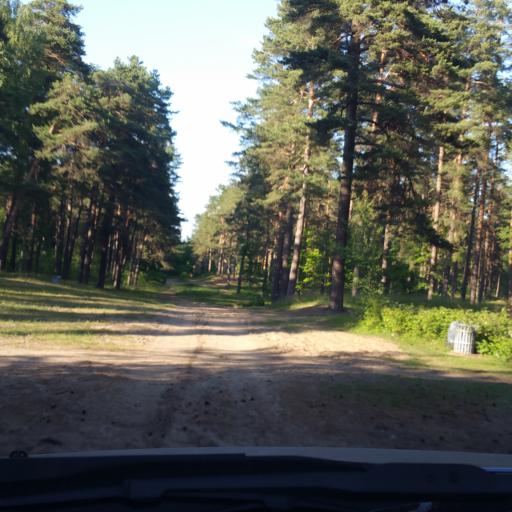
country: LV
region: Riga
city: Jaunciems
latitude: 56.9779
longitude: 24.2035
